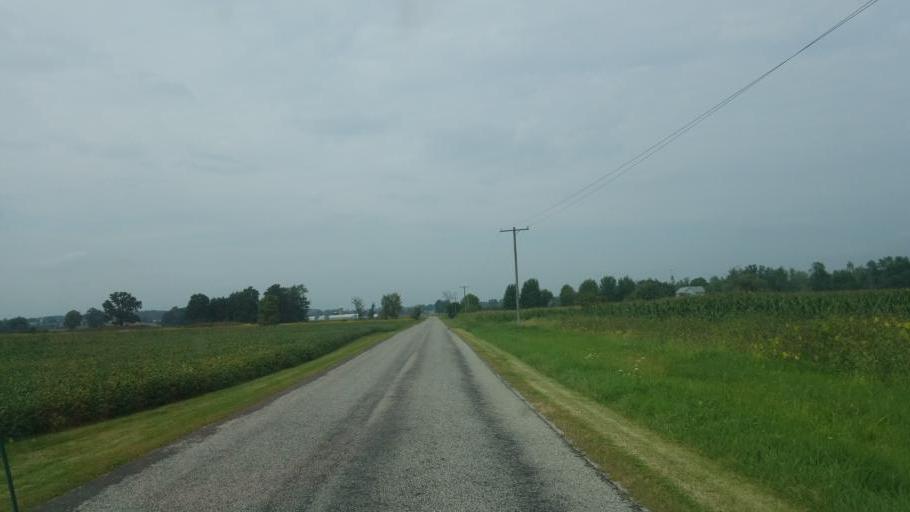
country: US
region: Ohio
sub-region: Wayne County
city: Rittman
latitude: 40.9486
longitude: -81.8120
